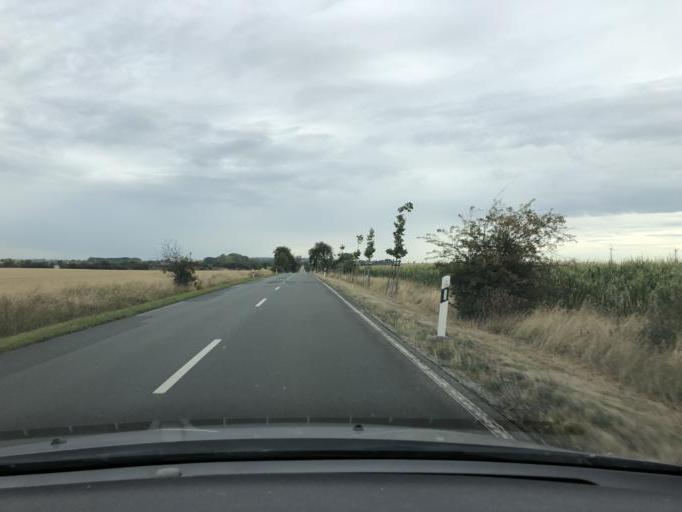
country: DE
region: Saxony-Anhalt
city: Brumby
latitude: 51.8745
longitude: 11.7124
